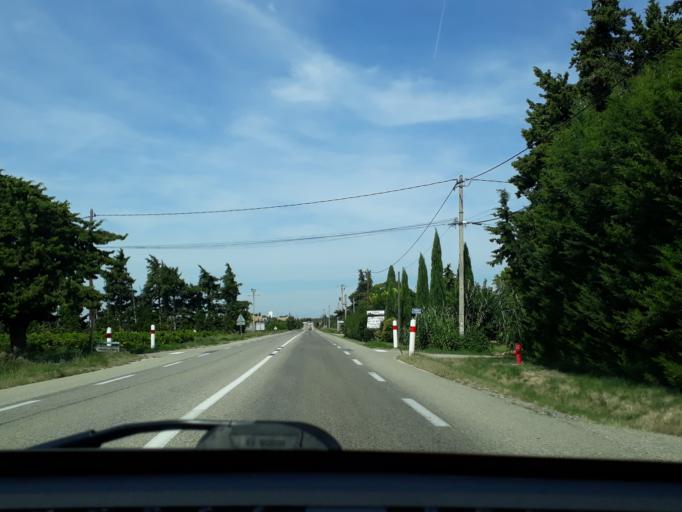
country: FR
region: Provence-Alpes-Cote d'Azur
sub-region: Departement du Vaucluse
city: Violes
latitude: 44.1764
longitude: 4.9586
